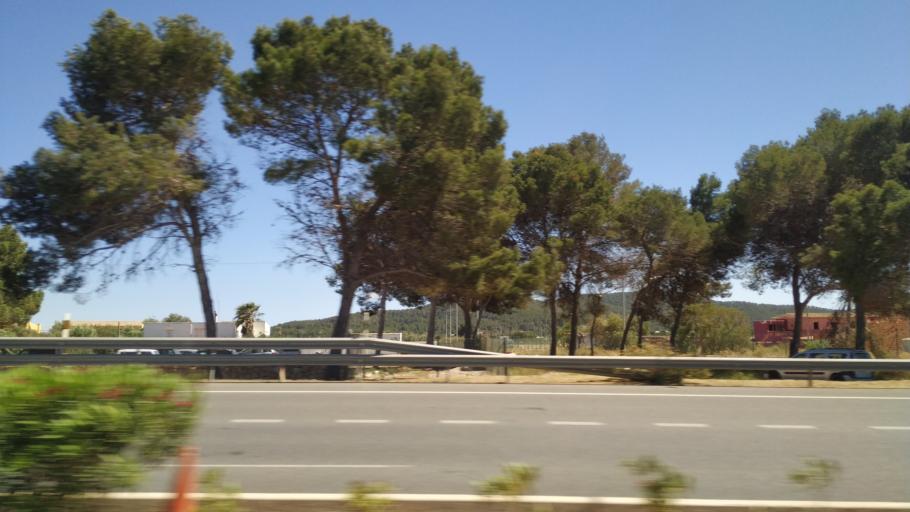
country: ES
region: Balearic Islands
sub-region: Illes Balears
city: Ibiza
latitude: 38.8833
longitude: 1.3880
